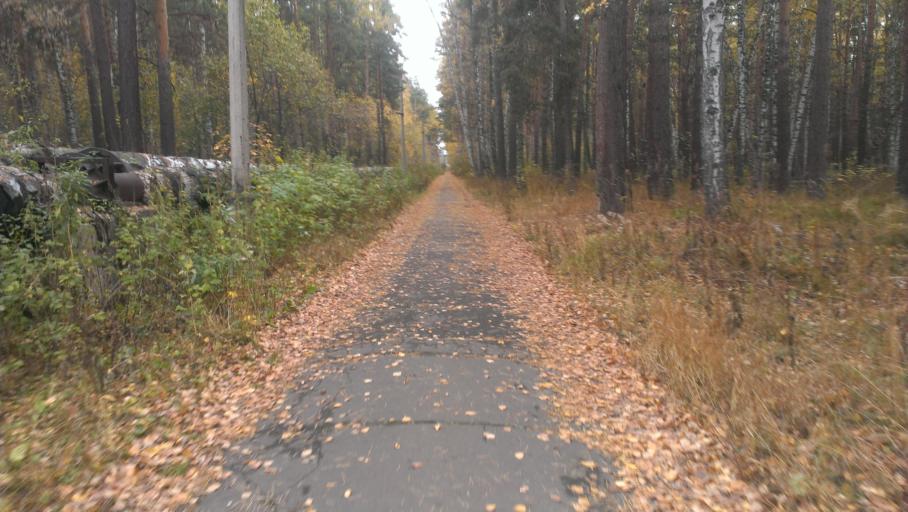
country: RU
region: Altai Krai
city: Yuzhnyy
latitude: 53.2621
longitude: 83.6871
